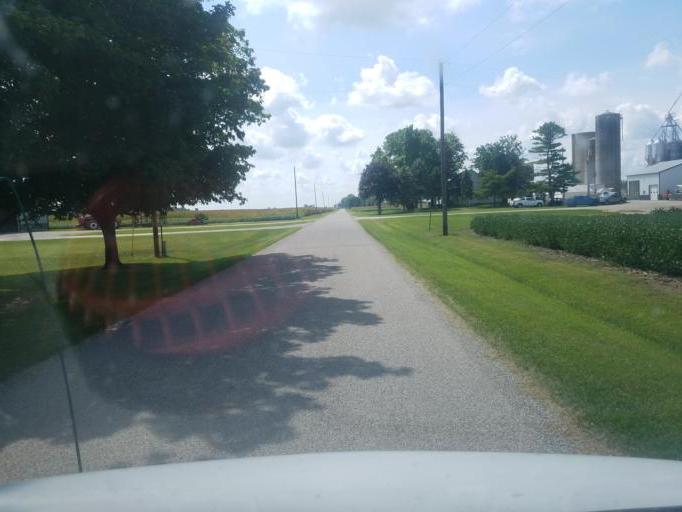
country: US
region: Ohio
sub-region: Marion County
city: Prospect
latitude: 40.4598
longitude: -83.1346
